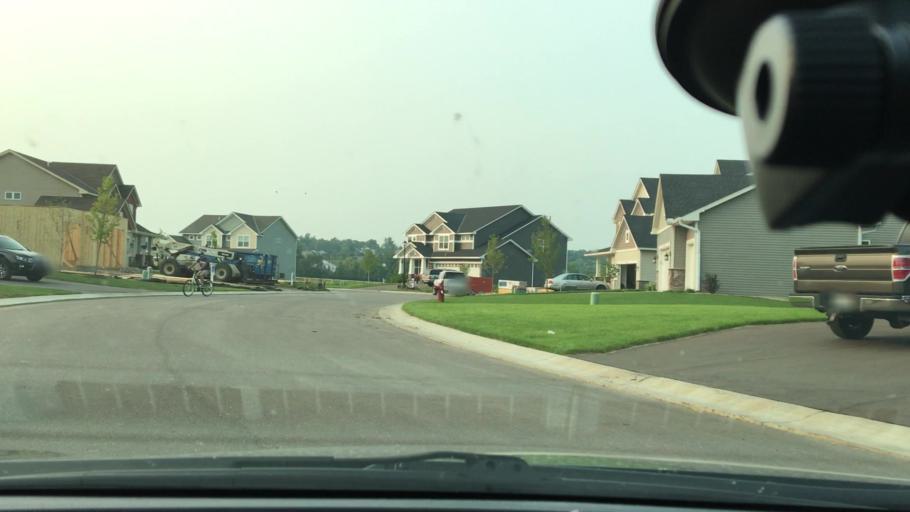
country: US
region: Minnesota
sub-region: Wright County
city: Saint Michael
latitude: 45.2087
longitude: -93.6309
